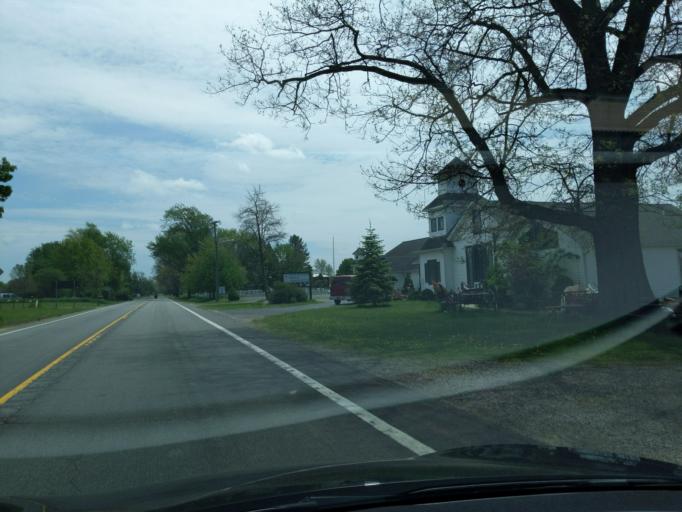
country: US
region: Michigan
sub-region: Ingham County
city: Stockbridge
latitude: 42.5097
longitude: -84.1583
